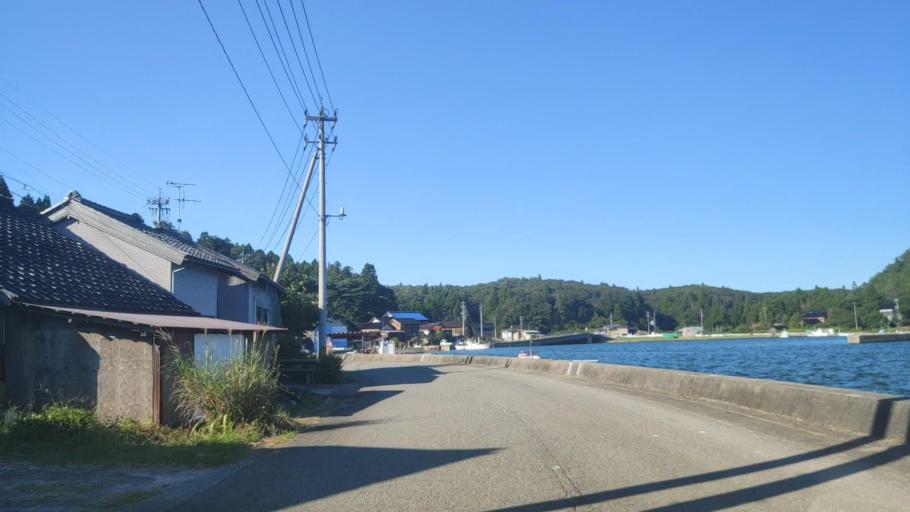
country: JP
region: Ishikawa
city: Nanao
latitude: 37.1129
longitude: 136.8820
